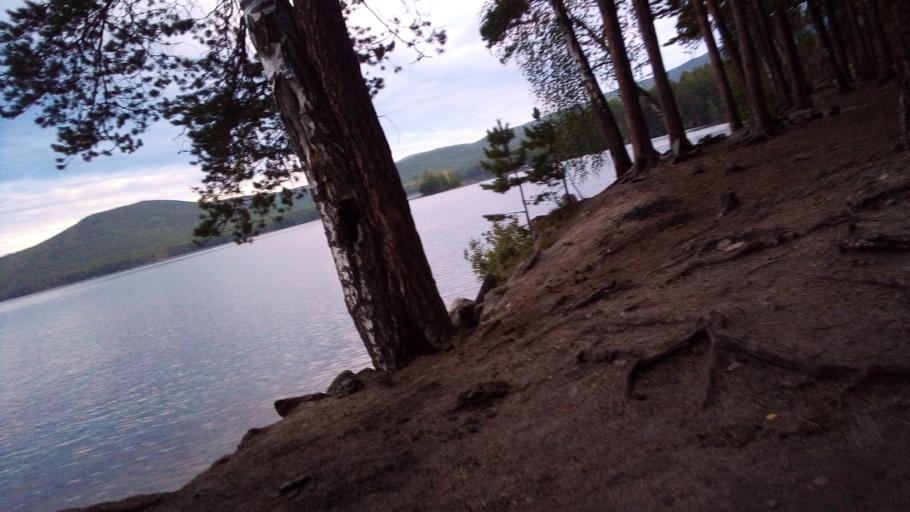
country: RU
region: Chelyabinsk
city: Turgoyak
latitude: 55.1775
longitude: 60.0265
